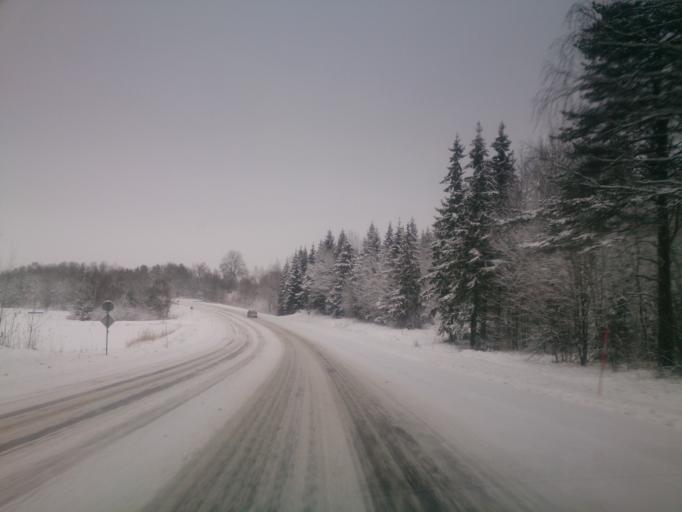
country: SE
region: OEstergoetland
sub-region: Norrkopings Kommun
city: Kimstad
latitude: 58.5038
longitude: 15.9792
